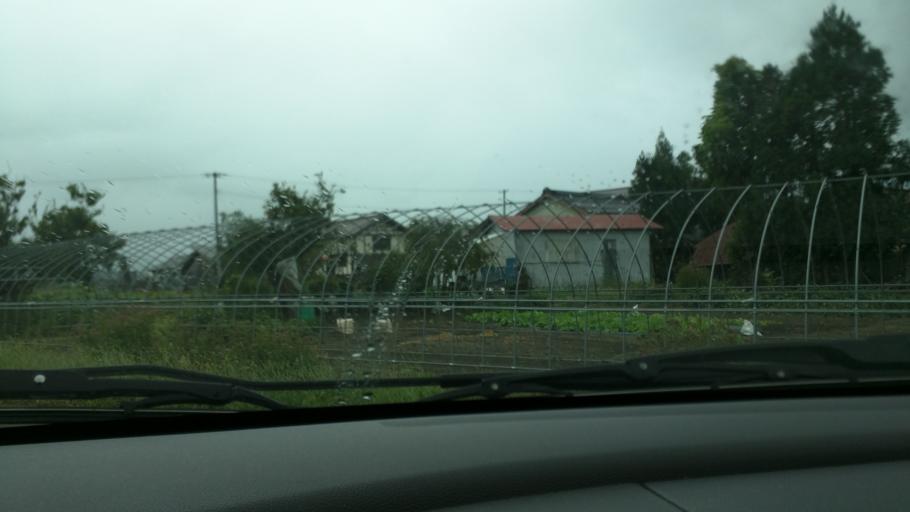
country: JP
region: Fukushima
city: Kitakata
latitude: 37.4630
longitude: 139.8579
